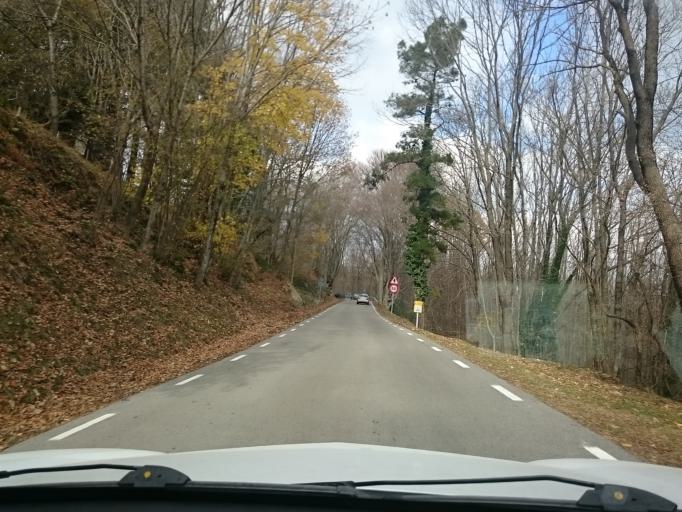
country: ES
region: Catalonia
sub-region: Provincia de Barcelona
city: Fogars de Montclus
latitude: 41.7676
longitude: 2.4665
